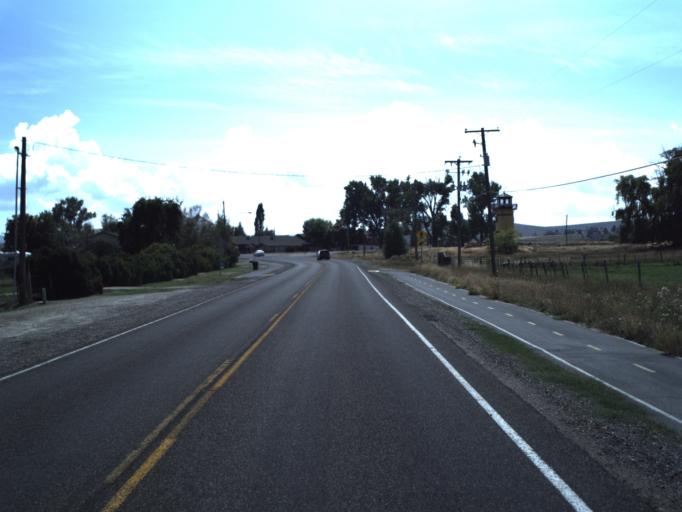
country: US
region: Idaho
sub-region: Bear Lake County
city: Paris
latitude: 41.9121
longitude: -111.3910
